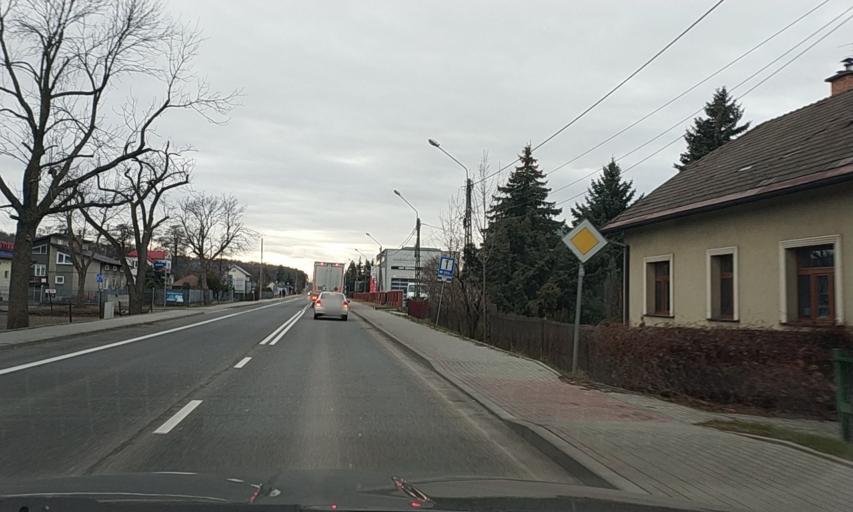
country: PL
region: Lesser Poland Voivodeship
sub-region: Powiat tarnowski
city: Koszyce Wielkie
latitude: 49.9941
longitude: 20.9417
